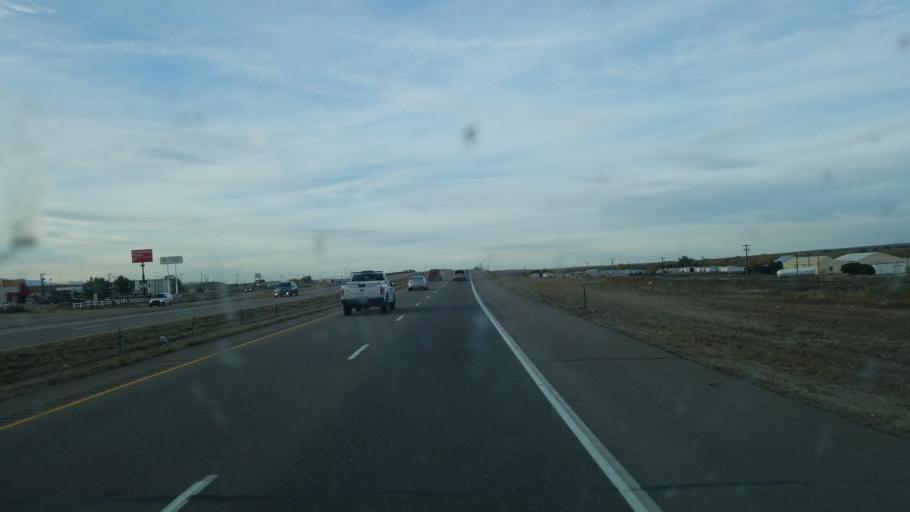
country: US
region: Colorado
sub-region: Pueblo County
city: Pueblo
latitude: 38.3397
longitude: -104.6197
